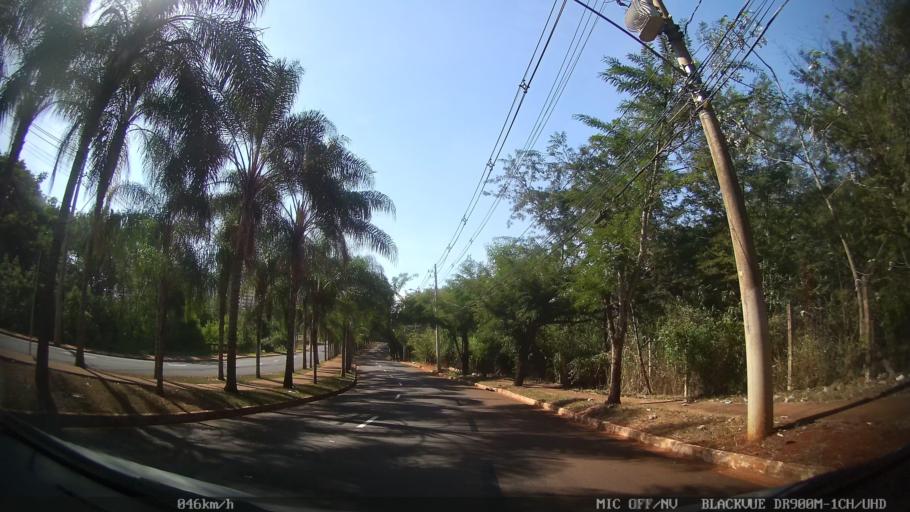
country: BR
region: Sao Paulo
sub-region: Ribeirao Preto
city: Ribeirao Preto
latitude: -21.2240
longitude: -47.8316
